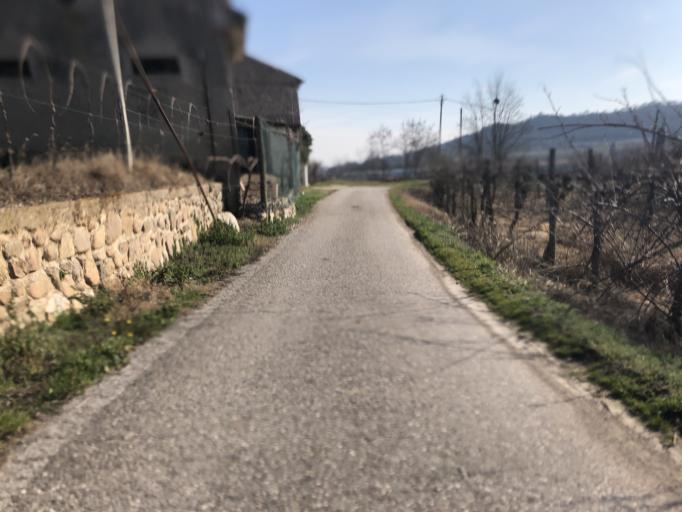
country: IT
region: Veneto
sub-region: Provincia di Verona
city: Valeggio sul Mincio
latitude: 45.3810
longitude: 10.7542
